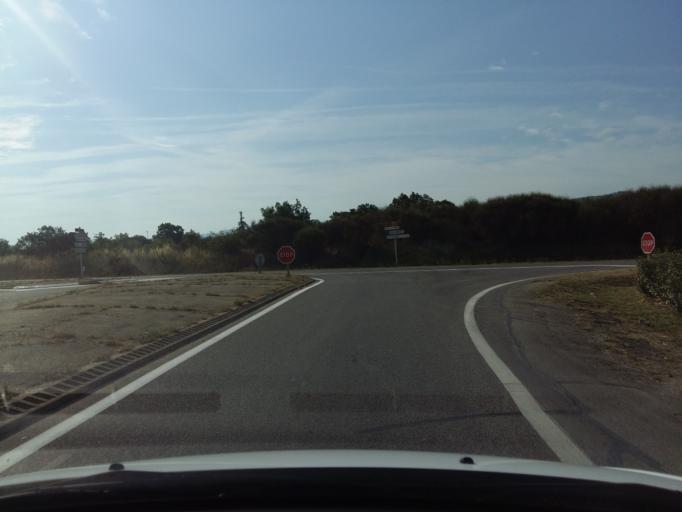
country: FR
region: Provence-Alpes-Cote d'Azur
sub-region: Departement du Vaucluse
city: Gargas
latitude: 43.8829
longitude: 5.3511
